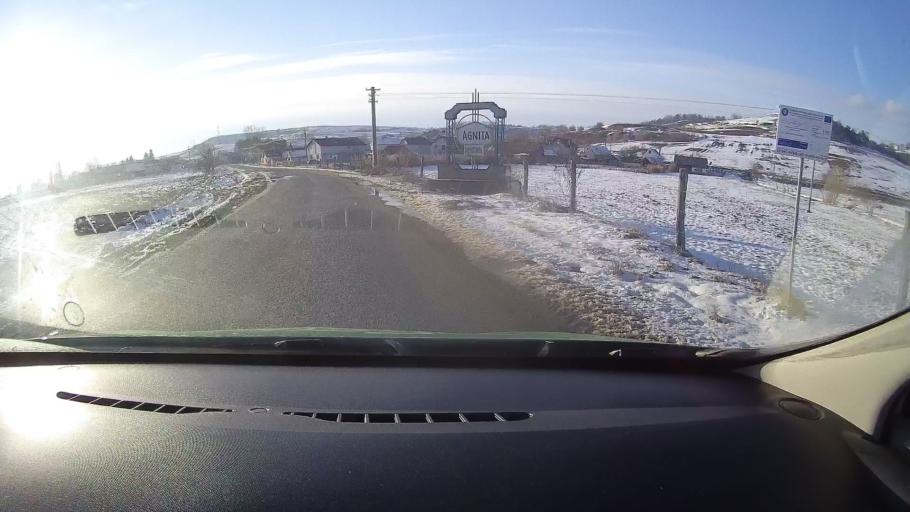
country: RO
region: Sibiu
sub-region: Oras Agnita
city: Ruja
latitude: 45.9840
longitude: 24.6493
